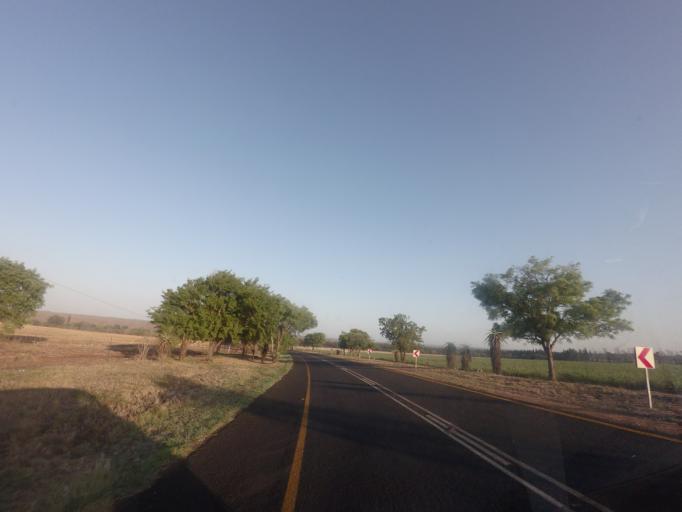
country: ZA
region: Mpumalanga
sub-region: Ehlanzeni District
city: Komatipoort
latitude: -25.3670
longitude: 31.9016
